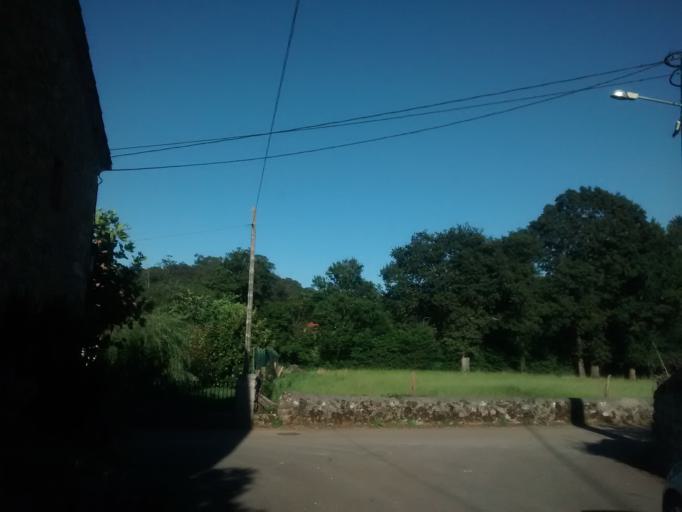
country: ES
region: Cantabria
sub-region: Provincia de Cantabria
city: Entrambasaguas
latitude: 43.3642
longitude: -3.6876
